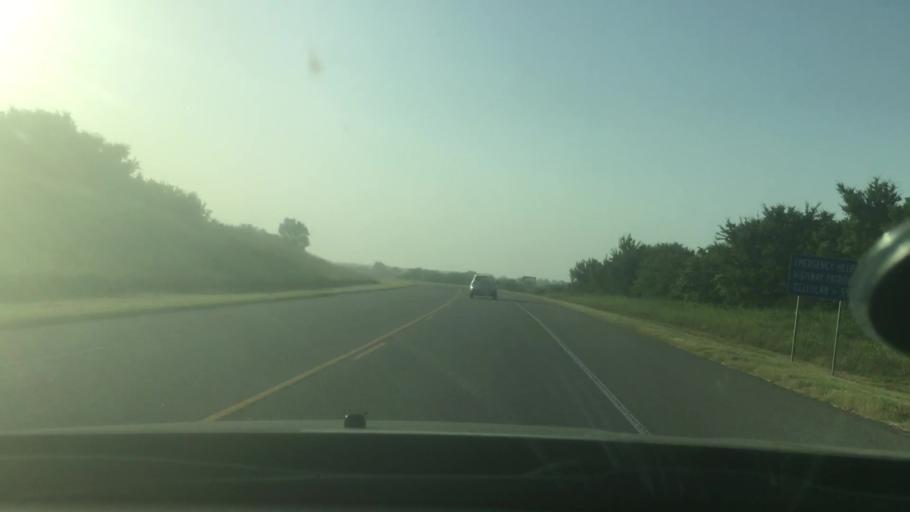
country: US
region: Oklahoma
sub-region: Pontotoc County
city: Ada
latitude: 34.6446
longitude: -96.5468
